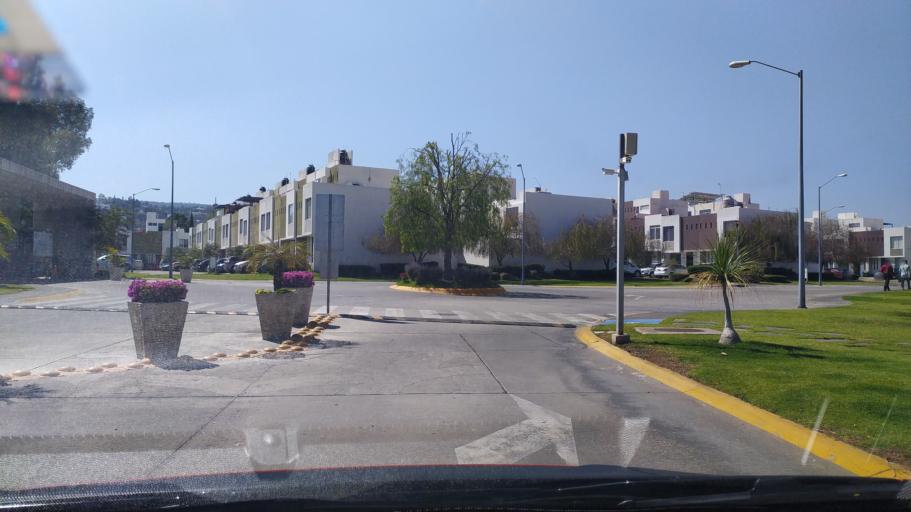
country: MX
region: Jalisco
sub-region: Tlajomulco de Zuniga
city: Palomar
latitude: 20.6300
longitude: -103.4643
